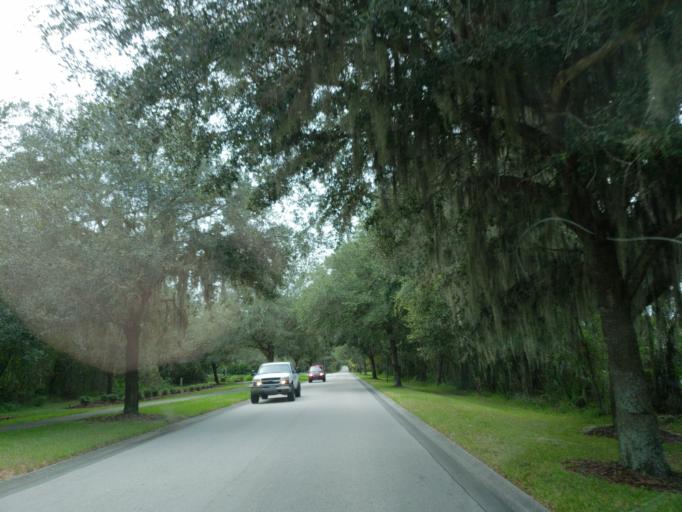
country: US
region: Florida
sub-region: Hillsborough County
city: Fish Hawk
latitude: 27.8428
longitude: -82.2225
